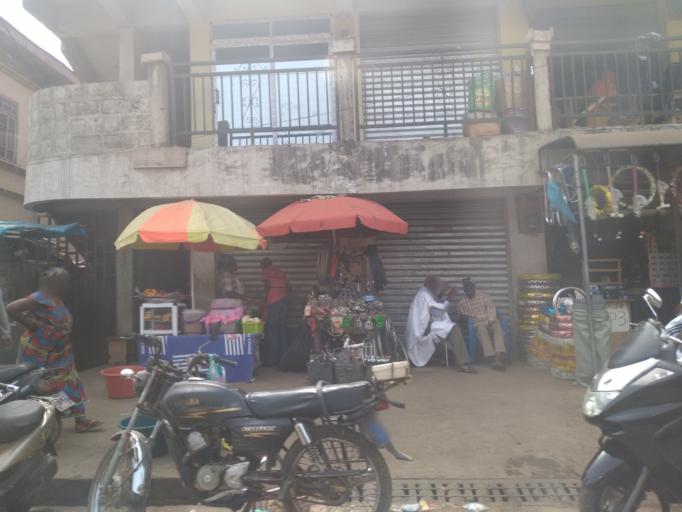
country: GH
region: Ashanti
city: Kumasi
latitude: 6.6997
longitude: -1.6174
